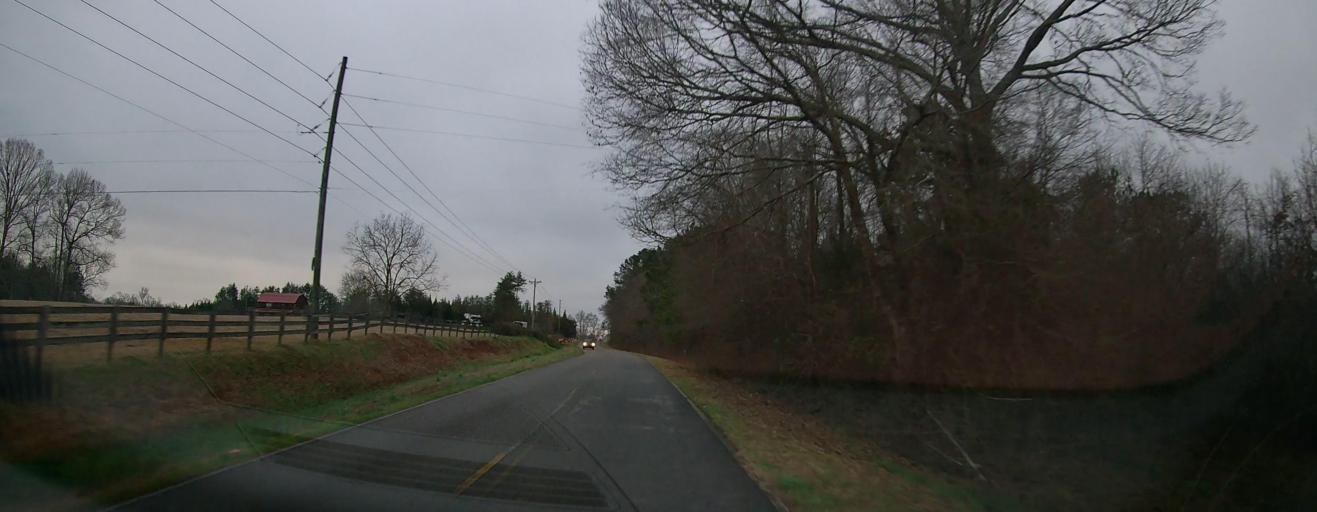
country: US
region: Georgia
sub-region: Lamar County
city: Barnesville
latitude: 33.0265
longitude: -84.1125
